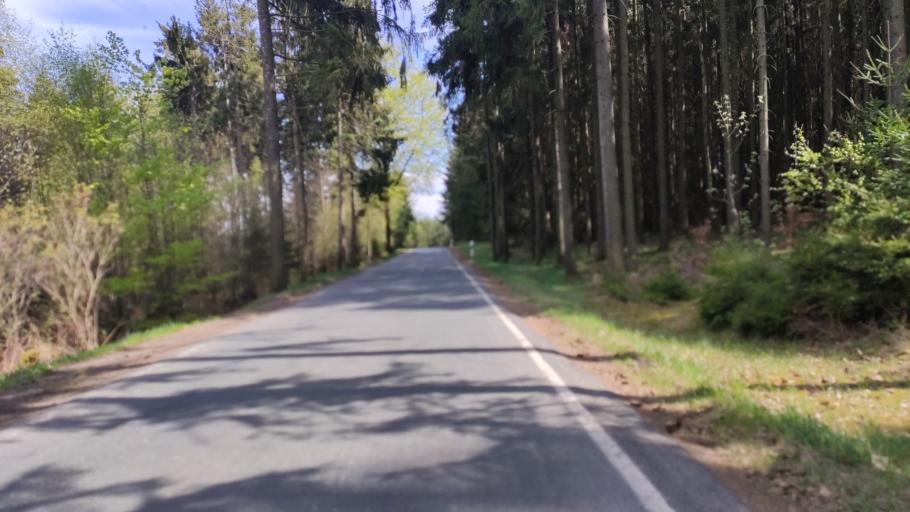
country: DE
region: Thuringia
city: Leutenberg
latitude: 50.5036
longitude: 11.4554
